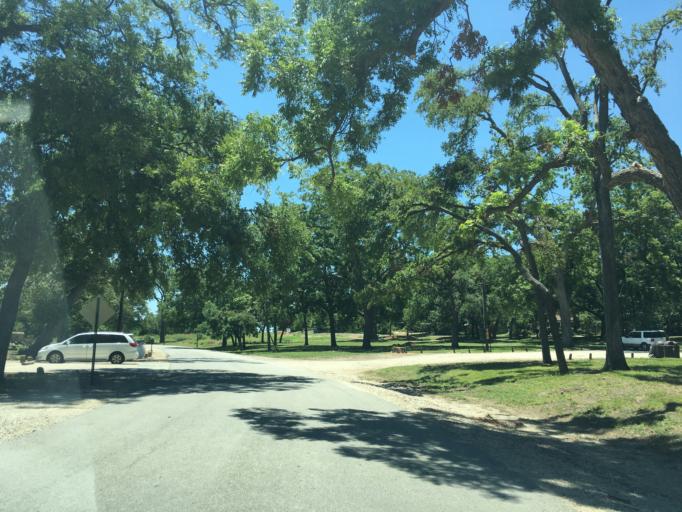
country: US
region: Texas
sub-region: Dallas County
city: Highland Park
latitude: 32.8392
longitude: -96.7087
